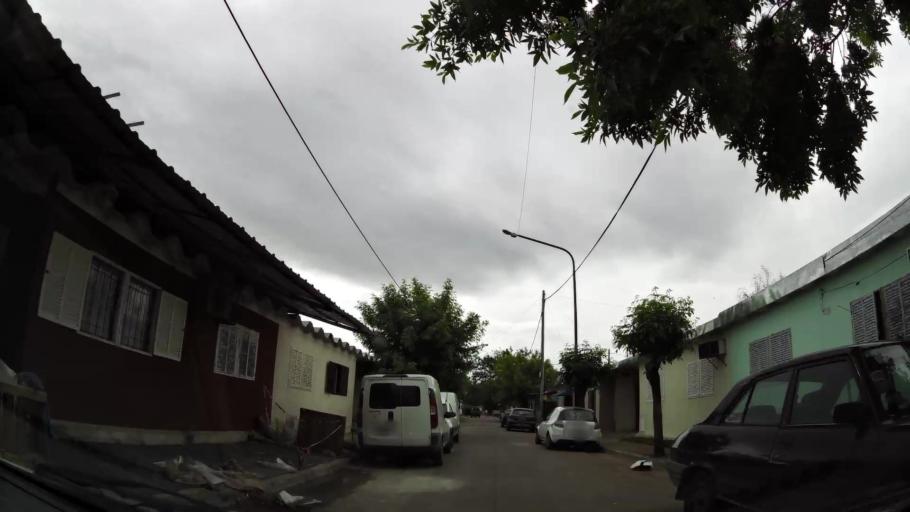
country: AR
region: Buenos Aires
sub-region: Partido de Quilmes
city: Quilmes
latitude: -34.7544
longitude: -58.2510
